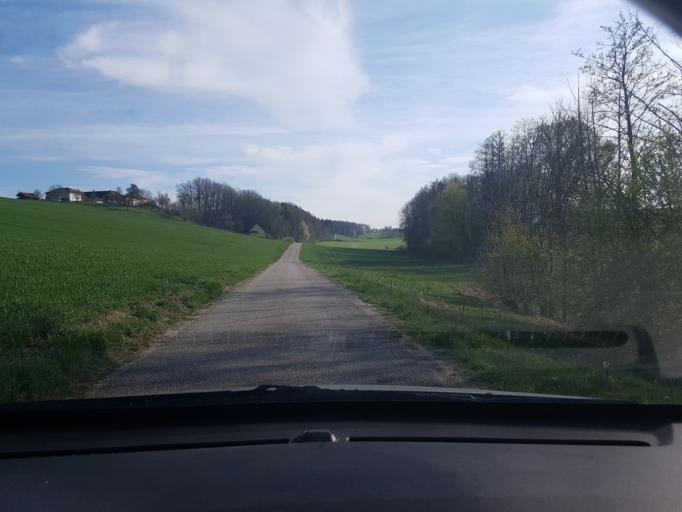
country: AT
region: Upper Austria
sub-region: Politischer Bezirk Linz-Land
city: Ansfelden
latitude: 48.1794
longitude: 14.3299
